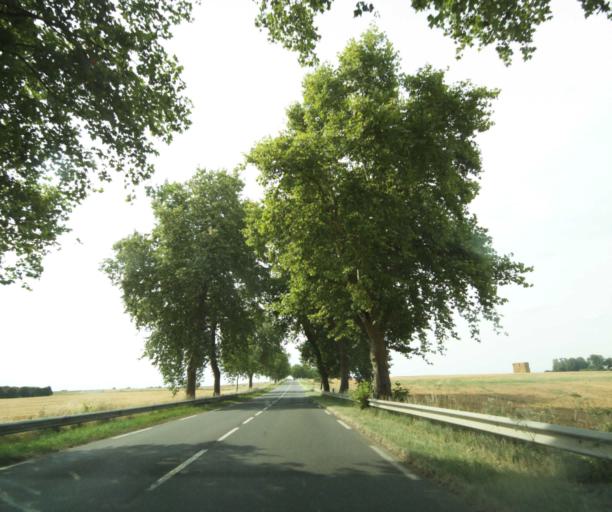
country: FR
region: Centre
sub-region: Departement d'Indre-et-Loire
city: Saint-Paterne-Racan
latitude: 47.6030
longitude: 0.5180
